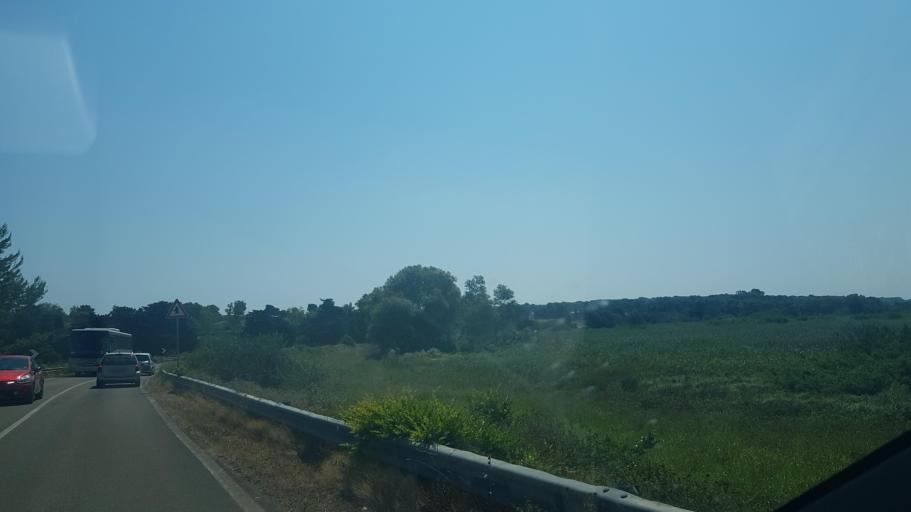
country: IT
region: Apulia
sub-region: Provincia di Lecce
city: Borgagne
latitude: 40.2249
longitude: 18.4368
